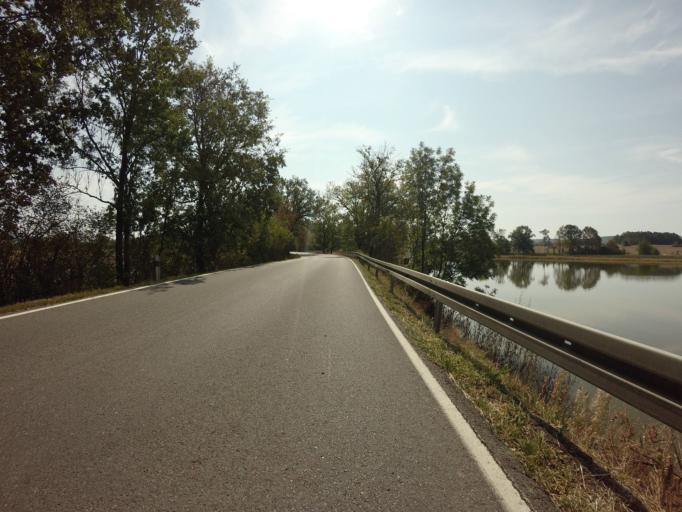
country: CZ
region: Central Bohemia
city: Sedlcany
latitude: 49.6178
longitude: 14.4104
